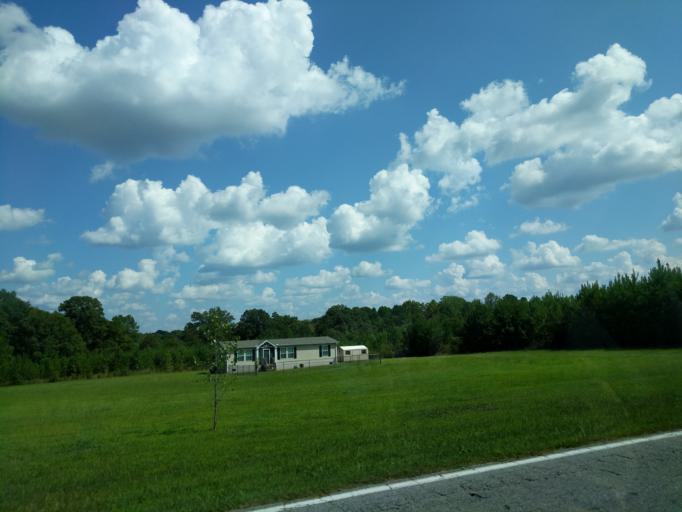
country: US
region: South Carolina
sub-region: Spartanburg County
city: Woodruff
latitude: 34.7191
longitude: -82.0453
